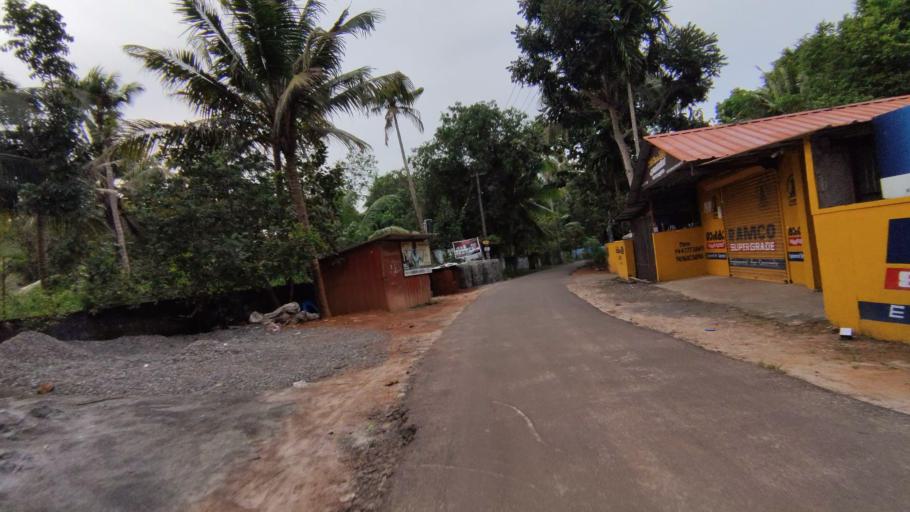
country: IN
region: Kerala
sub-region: Alappuzha
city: Shertallai
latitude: 9.6348
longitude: 76.3596
